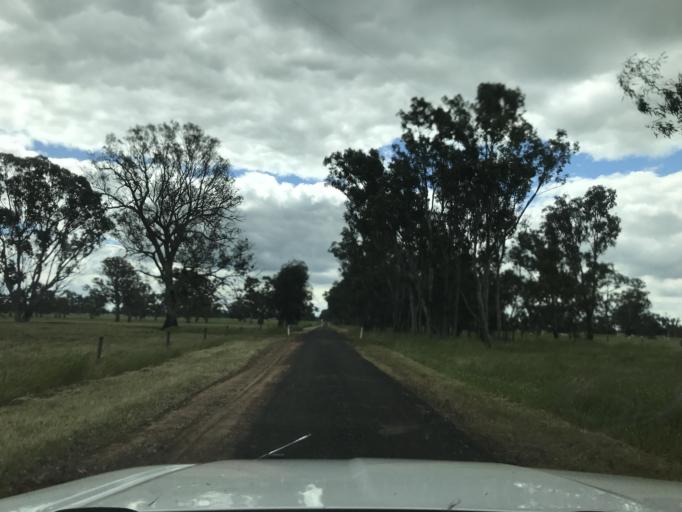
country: AU
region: South Australia
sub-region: Wattle Range
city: Penola
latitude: -37.0766
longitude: 141.1795
